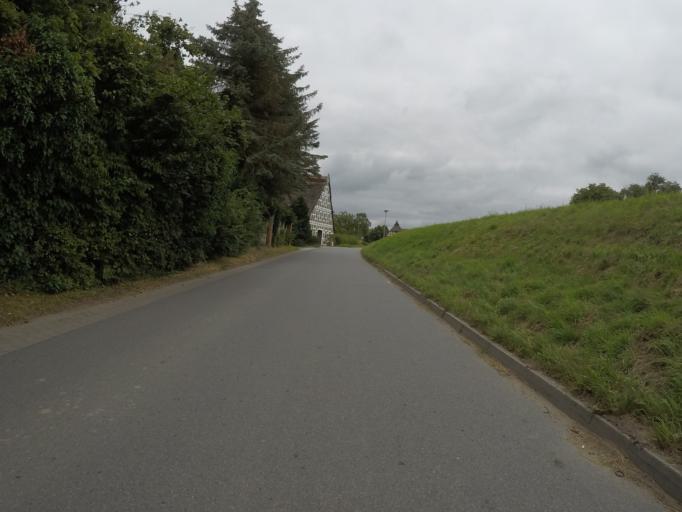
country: DE
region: Lower Saxony
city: Guderhandviertel
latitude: 53.5541
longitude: 9.6059
